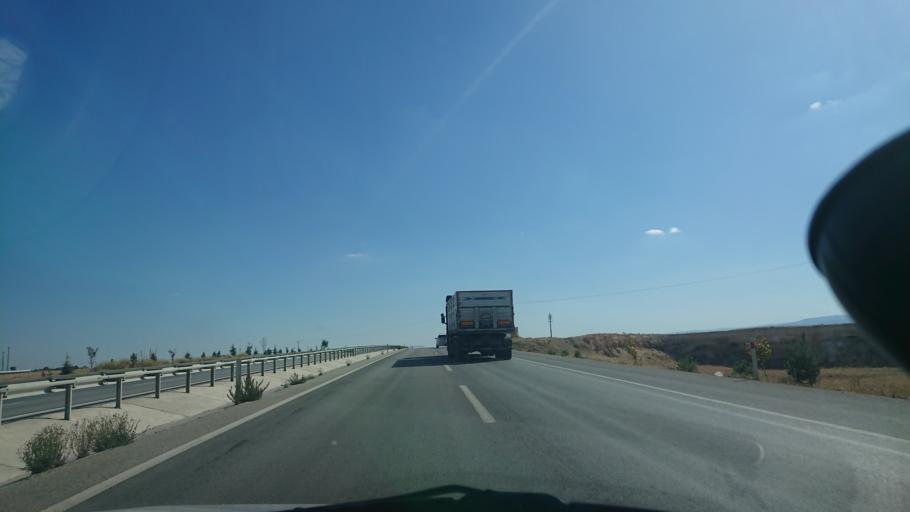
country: TR
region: Eskisehir
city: Mahmudiye
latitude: 39.5097
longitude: 30.9646
